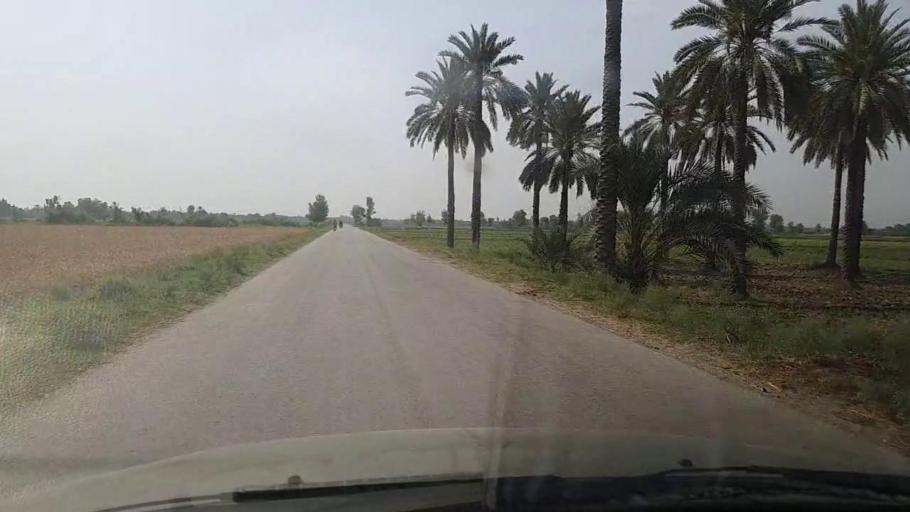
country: PK
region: Sindh
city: Gambat
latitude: 27.4663
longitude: 68.4782
